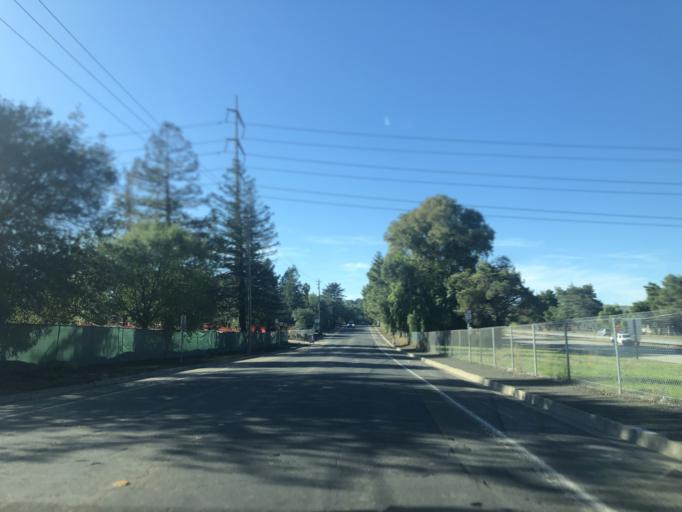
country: US
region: California
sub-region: Contra Costa County
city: Pacheco
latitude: 37.9905
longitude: -122.0890
